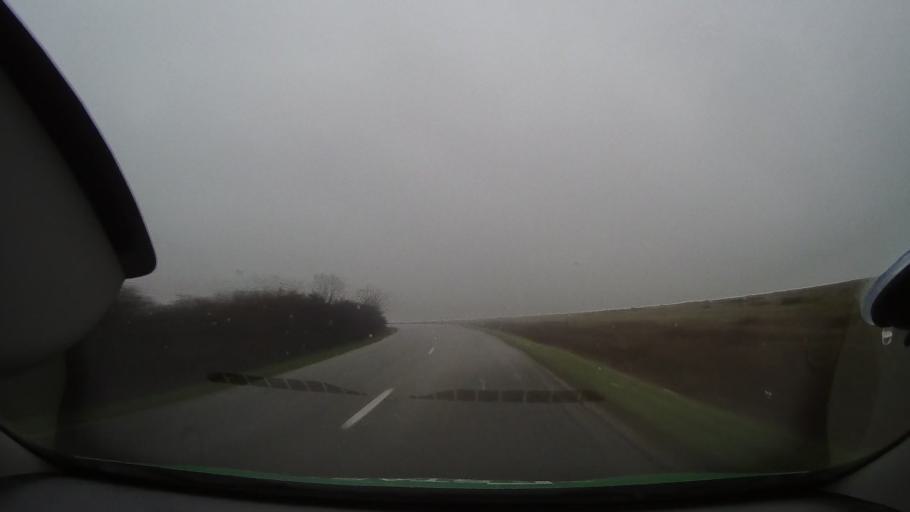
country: RO
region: Arad
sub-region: Comuna Craiova
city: Craiova
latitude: 46.6115
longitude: 21.9566
